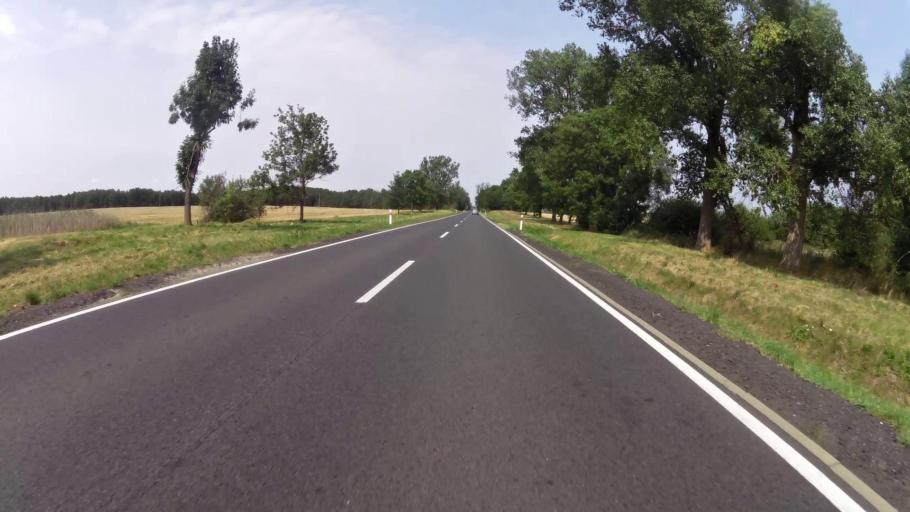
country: PL
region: West Pomeranian Voivodeship
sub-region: Powiat gryfinski
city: Mieszkowice
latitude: 52.8293
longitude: 14.4948
